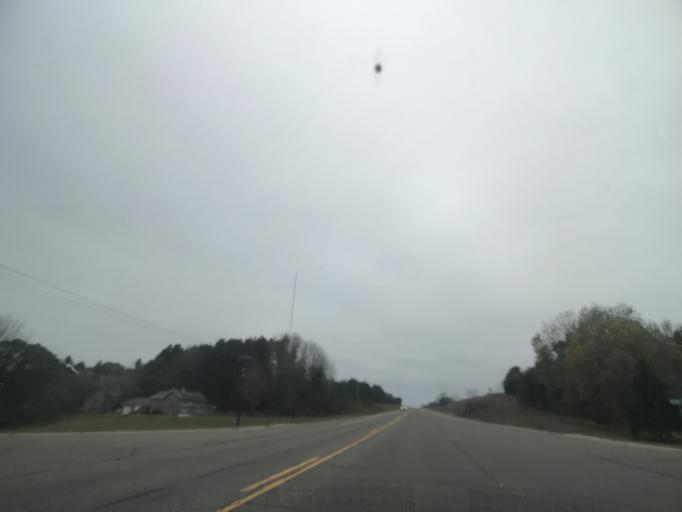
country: US
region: Wisconsin
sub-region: Oconto County
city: Gillett
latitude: 44.9991
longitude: -88.3872
